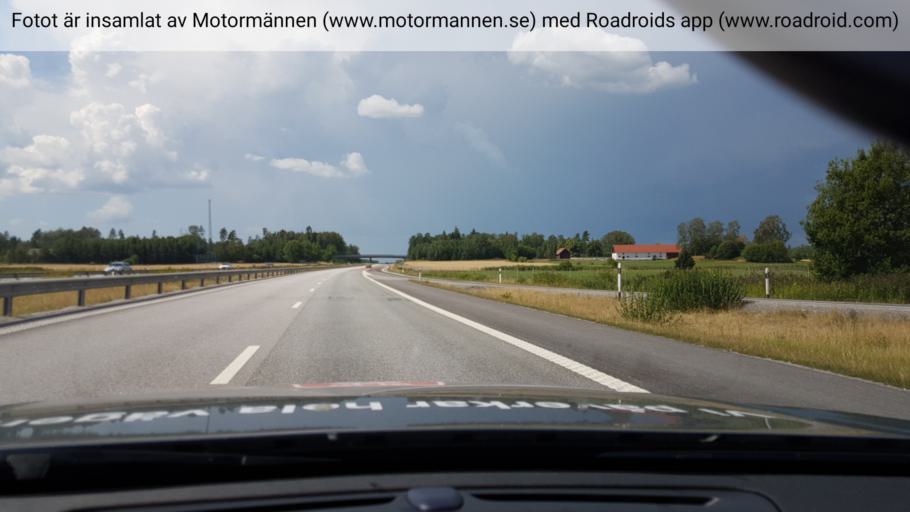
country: SE
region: OErebro
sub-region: Lindesbergs Kommun
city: Frovi
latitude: 59.3097
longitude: 15.4125
